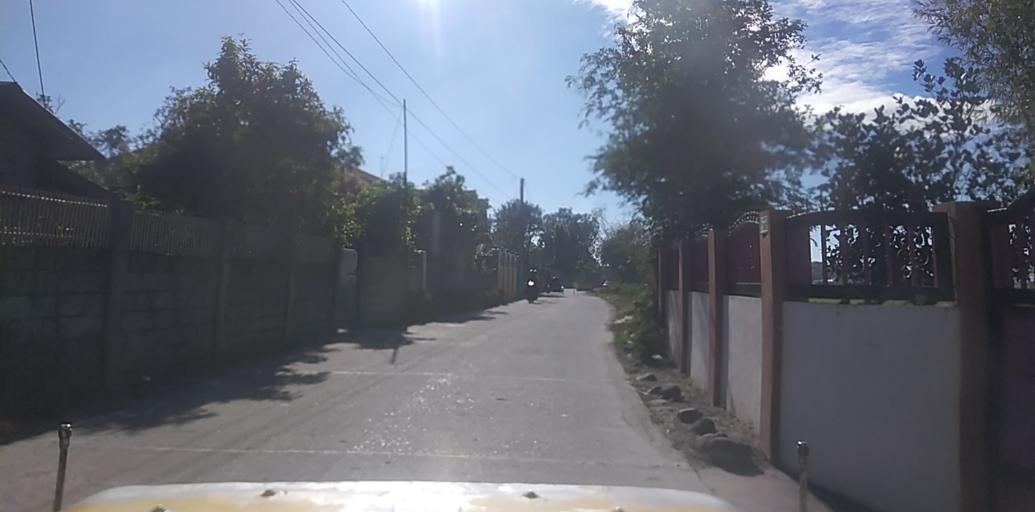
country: PH
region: Central Luzon
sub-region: Province of Pampanga
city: San Patricio
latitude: 15.1150
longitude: 120.7094
